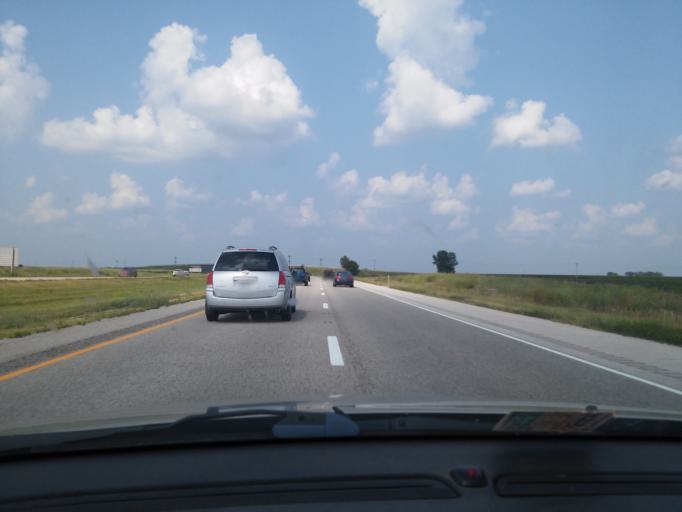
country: US
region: Illinois
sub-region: McLean County
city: Chenoa
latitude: 40.7602
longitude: -88.7227
